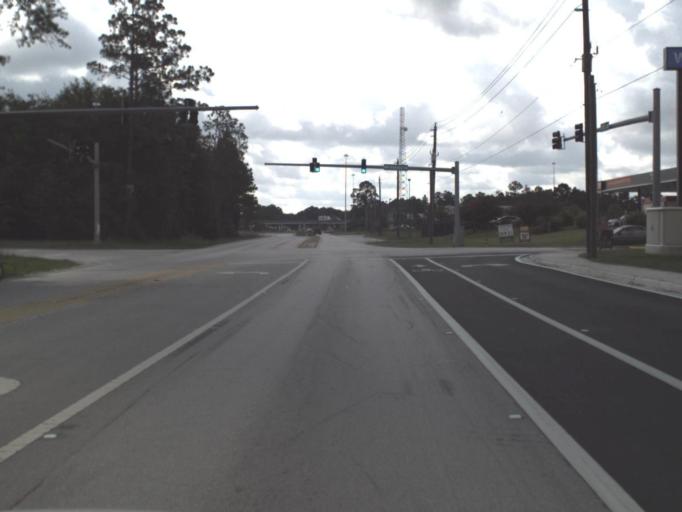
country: US
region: Florida
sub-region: Baker County
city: Macclenny
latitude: 30.2657
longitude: -82.1092
